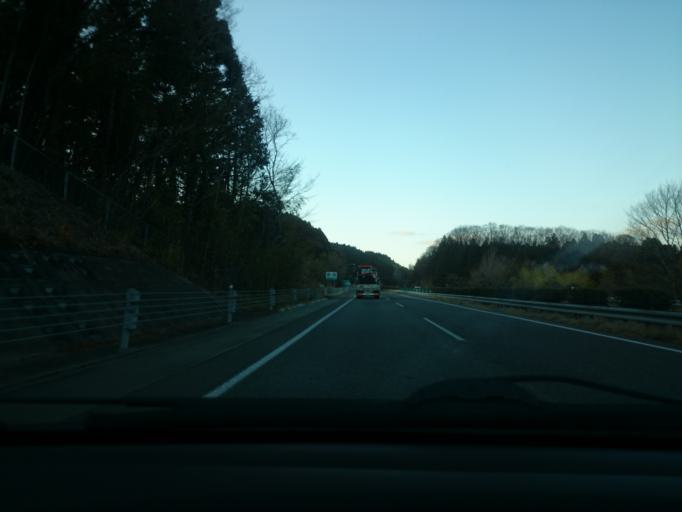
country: JP
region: Fukushima
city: Iwaki
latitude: 37.0151
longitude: 140.8139
